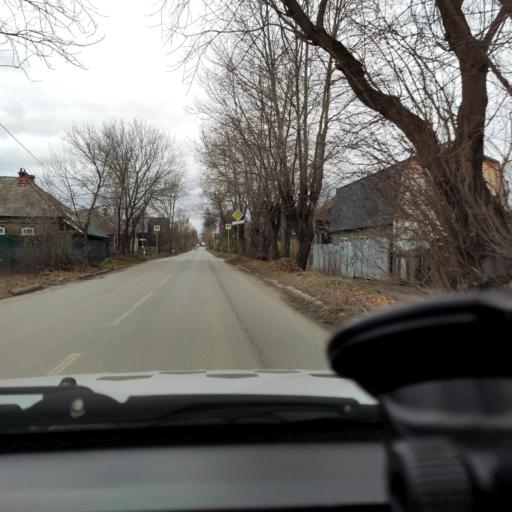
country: RU
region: Perm
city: Perm
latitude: 58.0134
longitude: 56.3194
